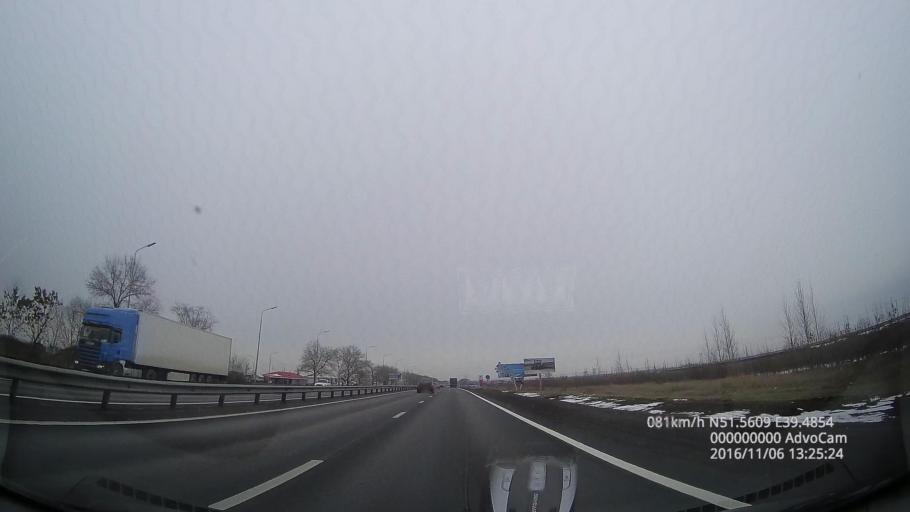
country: RU
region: Voronezj
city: Podkletnoye
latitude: 51.5575
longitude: 39.4886
